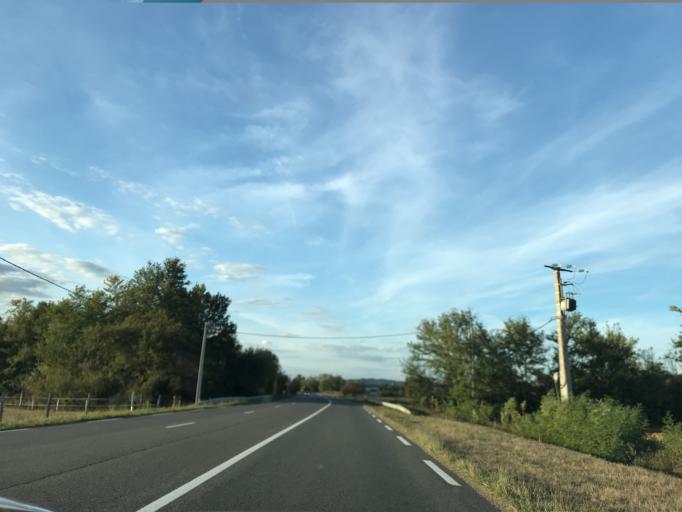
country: FR
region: Auvergne
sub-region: Departement de l'Allier
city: Saint-Yorre
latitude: 46.0380
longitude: 3.4751
